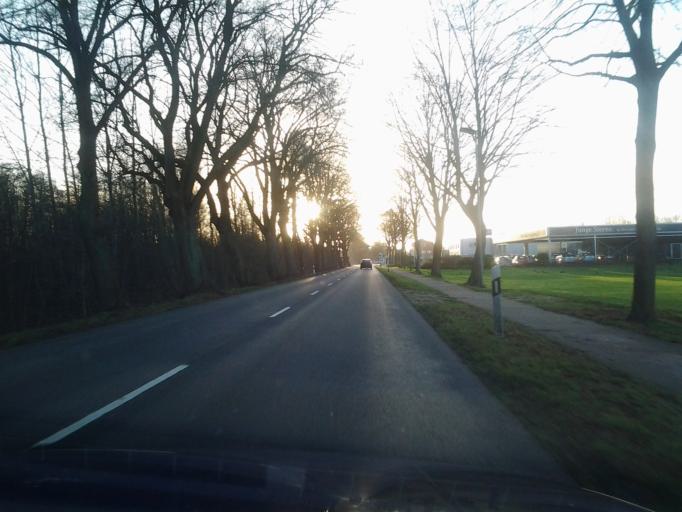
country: DE
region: Lower Saxony
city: Lilienthal
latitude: 53.1593
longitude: 8.9212
